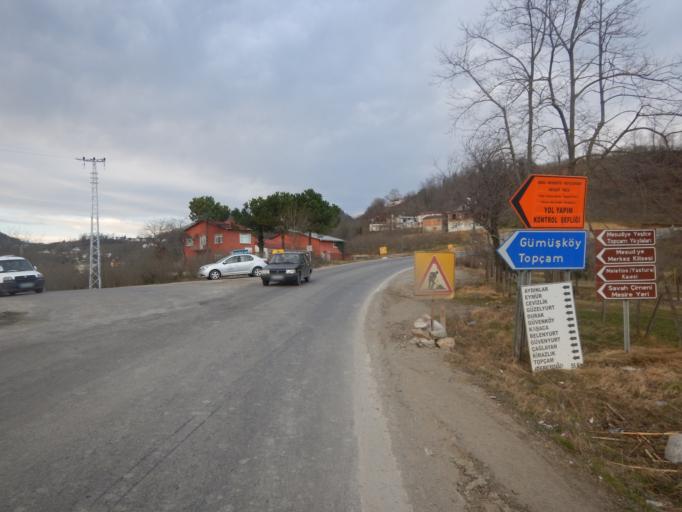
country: TR
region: Ordu
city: Uzunisa
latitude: 40.8988
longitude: 37.8215
